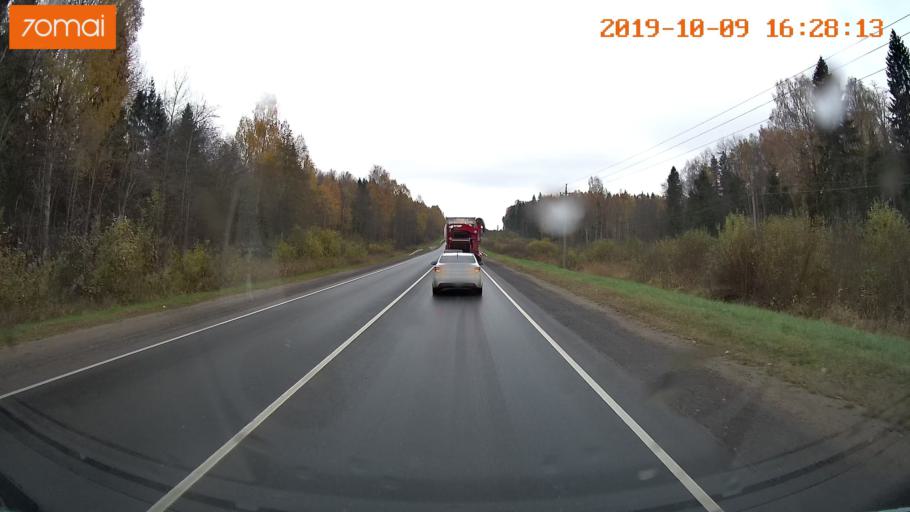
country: RU
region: Kostroma
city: Oktyabr'skiy
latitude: 57.6297
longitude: 40.9311
